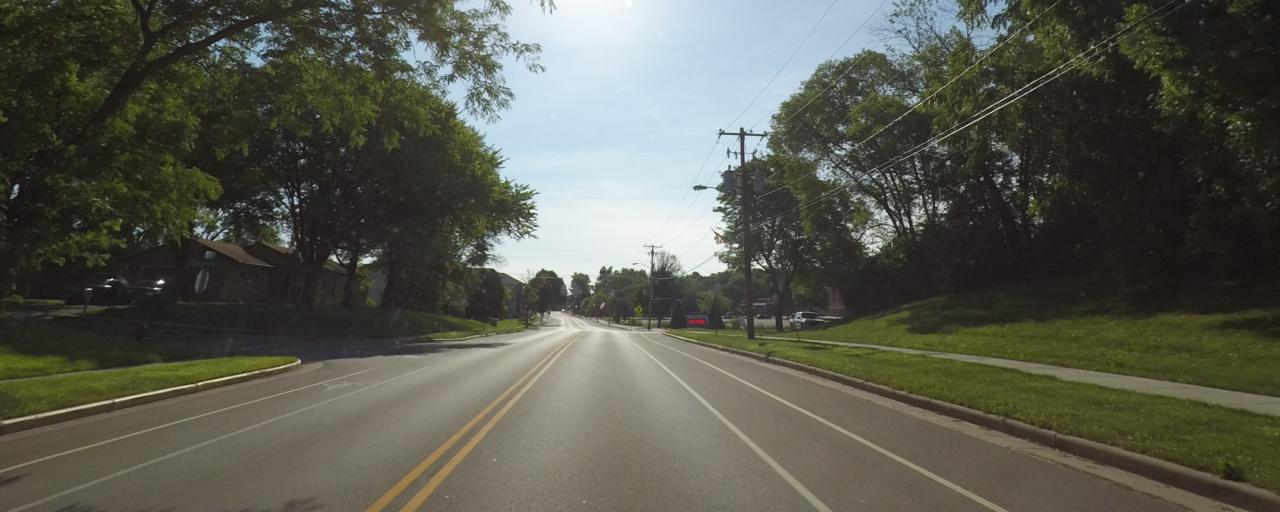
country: US
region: Wisconsin
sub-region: Dane County
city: McFarland
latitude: 43.0131
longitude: -89.2975
